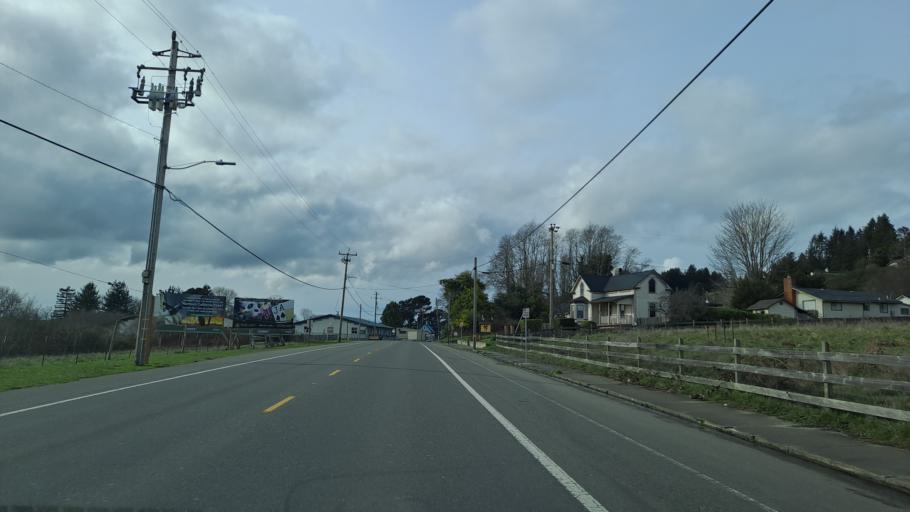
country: US
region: California
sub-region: Humboldt County
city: Fortuna
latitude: 40.5990
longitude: -124.1633
